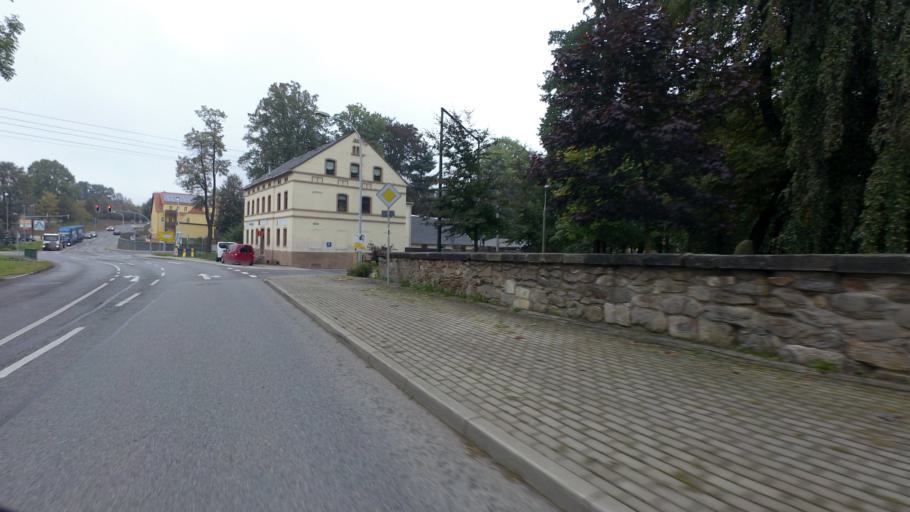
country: DE
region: Saxony
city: Neustadt in Sachsen
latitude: 51.0235
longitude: 14.2326
